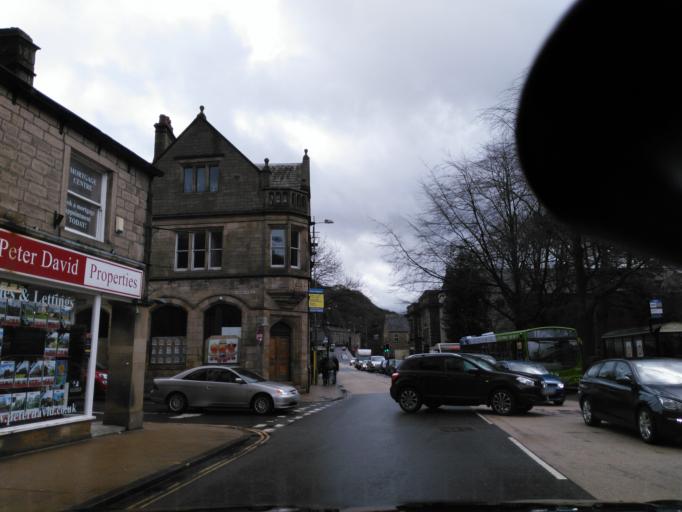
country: GB
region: England
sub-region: Calderdale
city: Hebden Bridge
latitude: 53.7411
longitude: -2.0136
